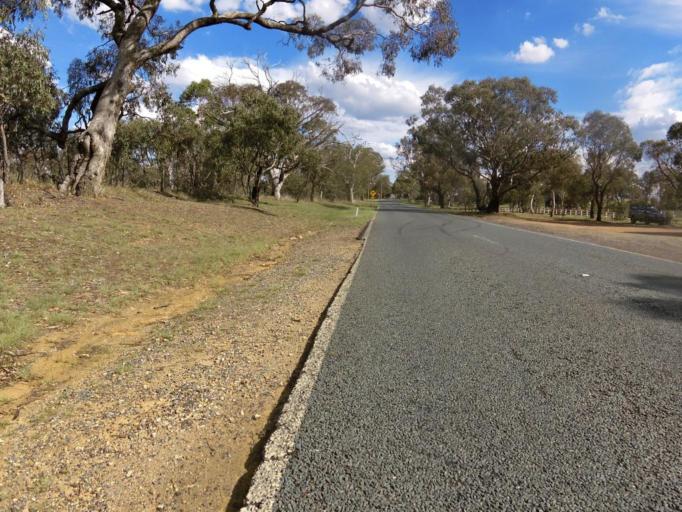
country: AU
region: Australian Capital Territory
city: Belconnen
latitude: -35.1787
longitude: 149.0729
